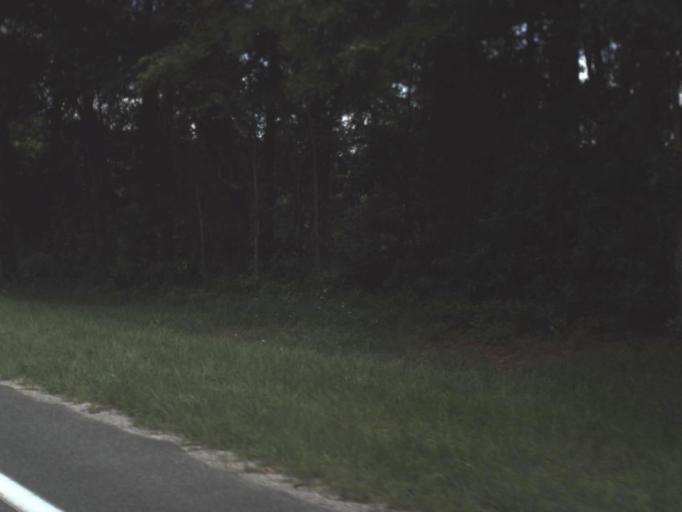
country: US
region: Florida
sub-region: Alachua County
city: High Springs
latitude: 29.8738
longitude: -82.6559
